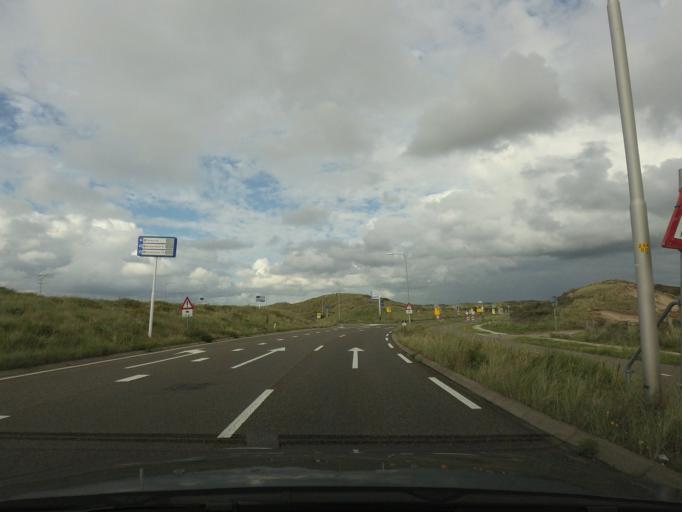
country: NL
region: North Holland
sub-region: Gemeente Zandvoort
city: Zandvoort
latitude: 52.4030
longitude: 4.5477
